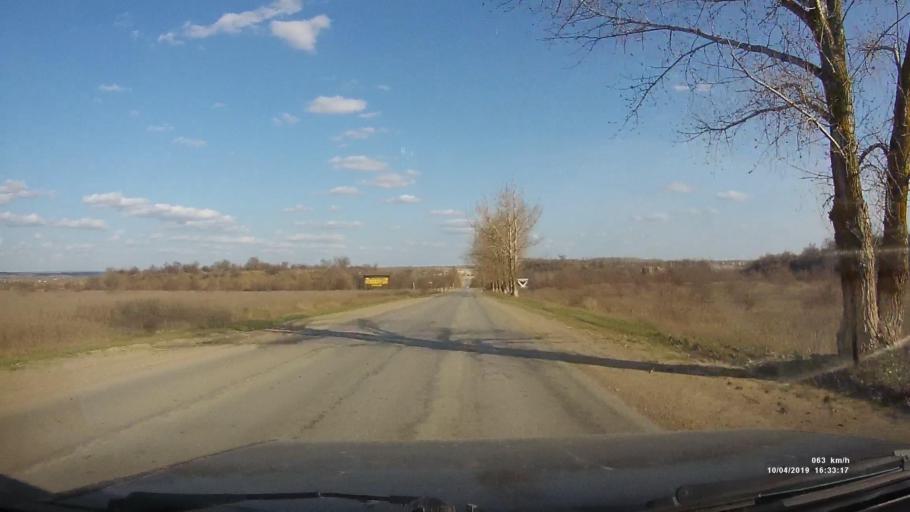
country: RU
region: Rostov
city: Staraya Stanitsa
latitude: 48.2422
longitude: 40.3961
